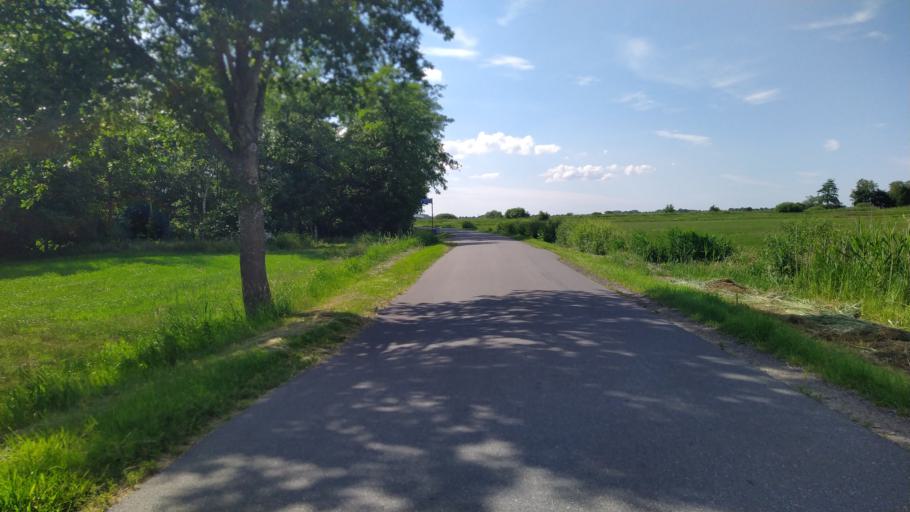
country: DE
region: Lower Saxony
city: Odisheim
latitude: 53.6700
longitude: 8.9206
